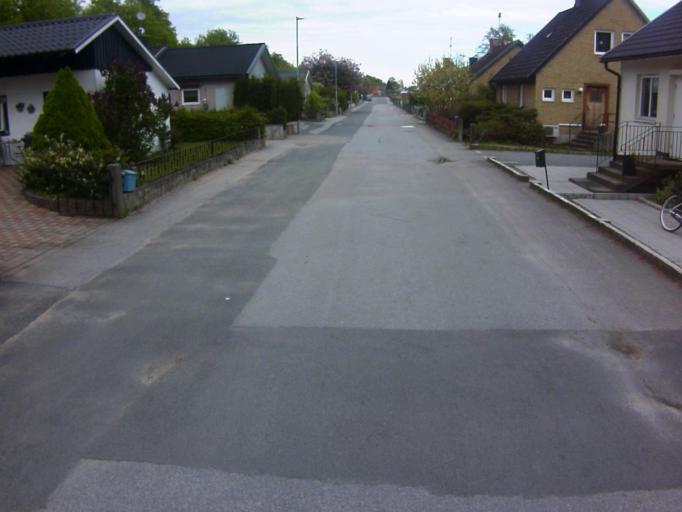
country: SE
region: Blekinge
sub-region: Solvesborgs Kommun
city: Soelvesborg
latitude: 56.0542
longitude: 14.5718
